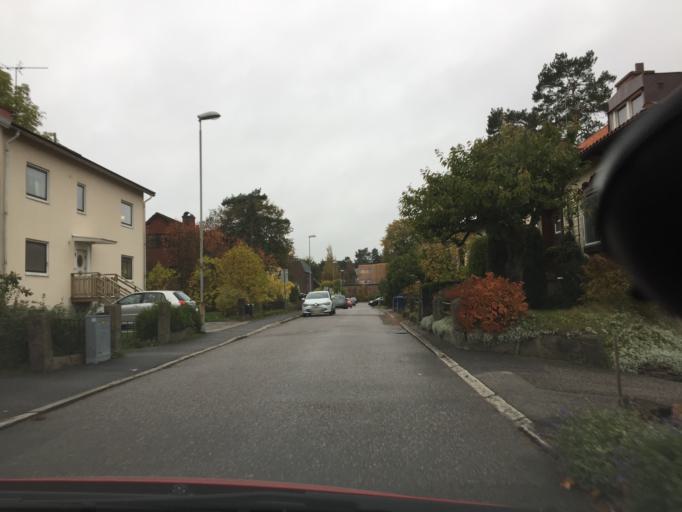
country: SE
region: Vaestra Goetaland
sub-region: Trollhattan
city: Trollhattan
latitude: 58.2805
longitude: 12.2939
